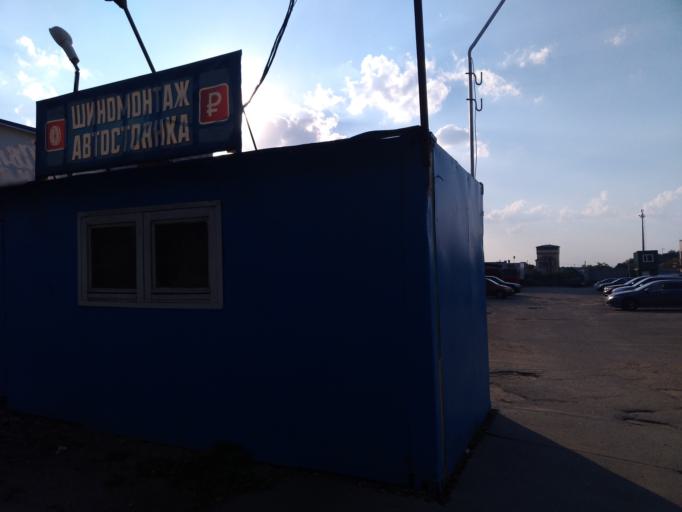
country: RU
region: Kaluga
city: Kaluga
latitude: 54.5229
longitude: 36.2527
